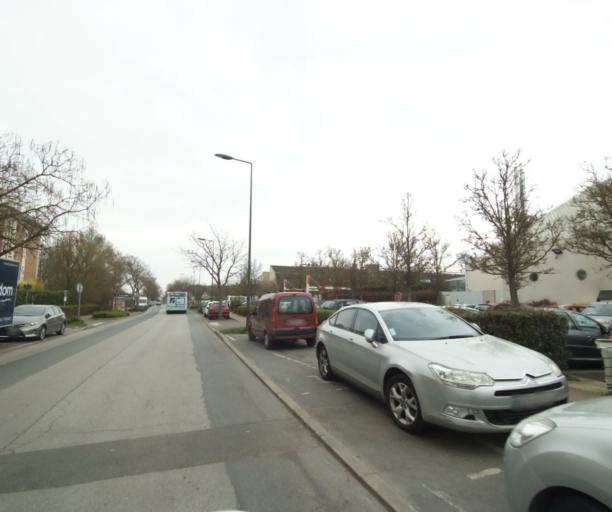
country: FR
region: Ile-de-France
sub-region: Departement du Val-d'Oise
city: Vaureal
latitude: 49.0456
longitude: 2.0303
